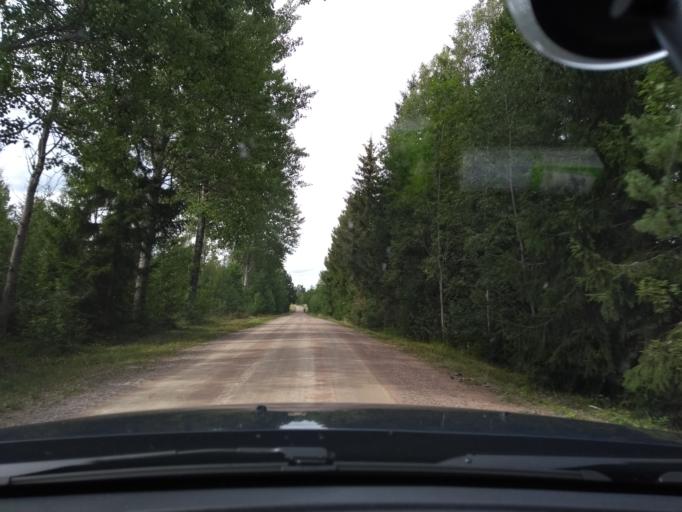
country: SE
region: Joenkoeping
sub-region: Eksjo Kommun
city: Mariannelund
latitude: 57.6281
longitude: 15.6403
